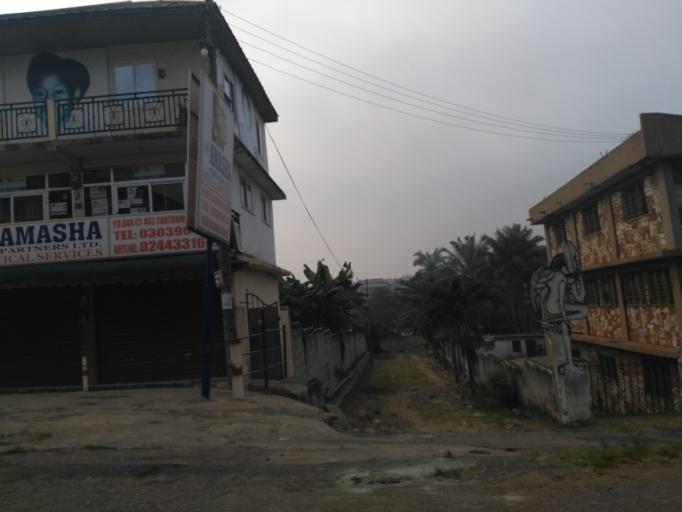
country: GH
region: Ashanti
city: Kumasi
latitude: 6.7076
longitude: -1.6072
